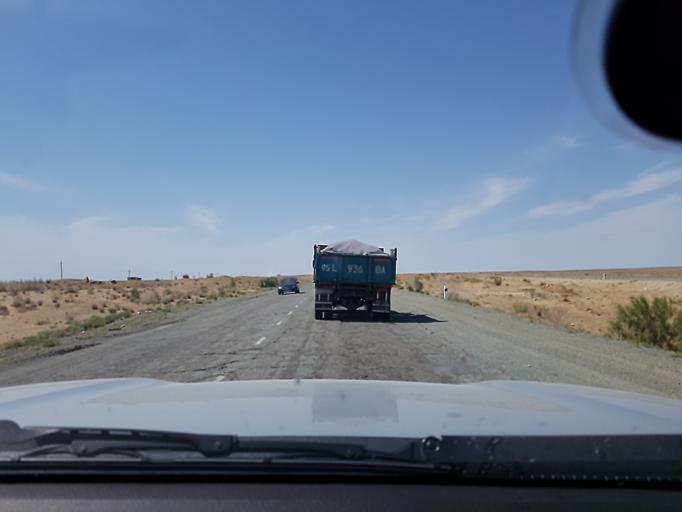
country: UZ
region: Karakalpakstan
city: Mang'it Shahri
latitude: 42.2878
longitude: 60.0771
